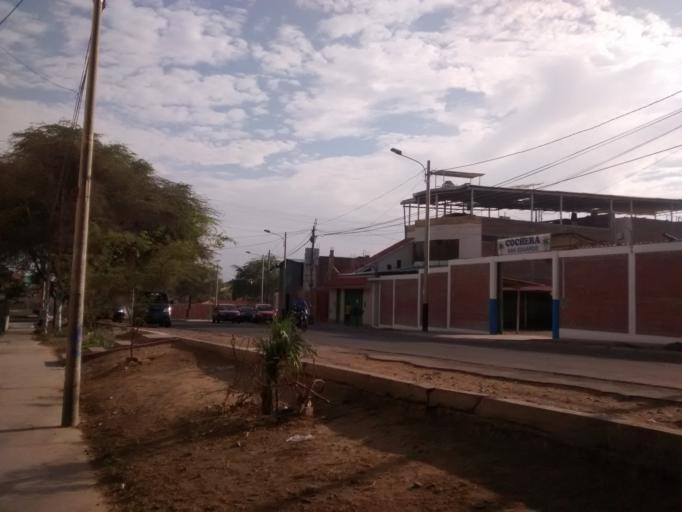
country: PE
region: Piura
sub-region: Provincia de Piura
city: Piura
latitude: -5.1741
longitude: -80.6315
